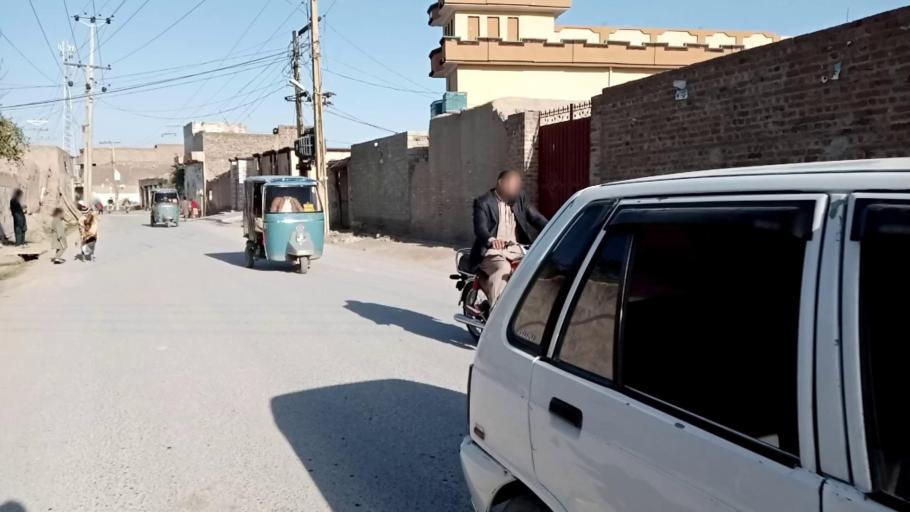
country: PK
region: Khyber Pakhtunkhwa
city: Peshawar
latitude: 34.0533
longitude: 71.5316
